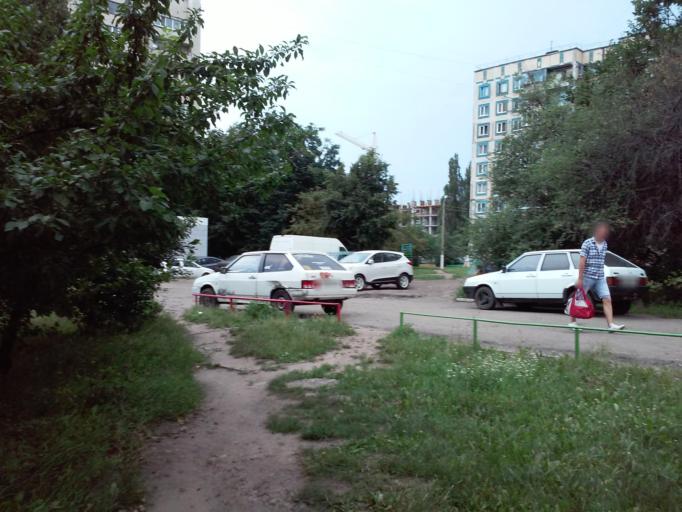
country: RU
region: Belgorod
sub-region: Belgorodskiy Rayon
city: Belgorod
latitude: 50.5719
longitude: 36.5815
